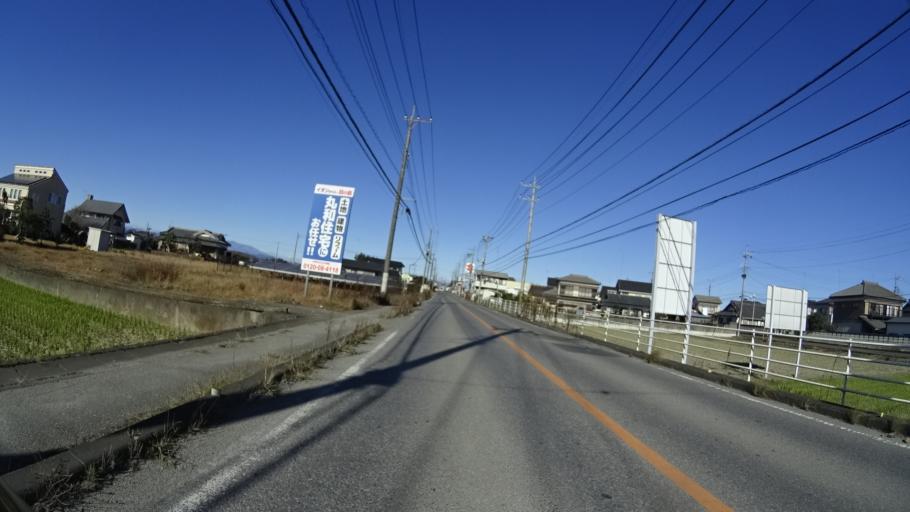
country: JP
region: Tochigi
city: Tochigi
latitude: 36.4168
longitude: 139.7492
